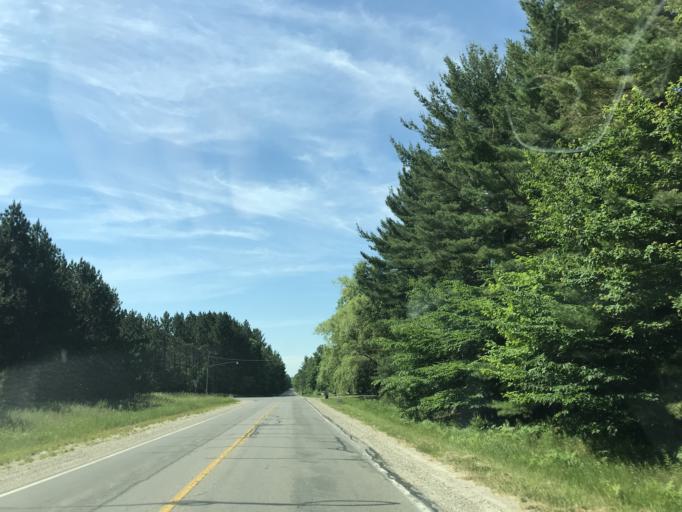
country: US
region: Michigan
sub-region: Grand Traverse County
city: Traverse City
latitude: 44.6554
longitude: -85.7170
